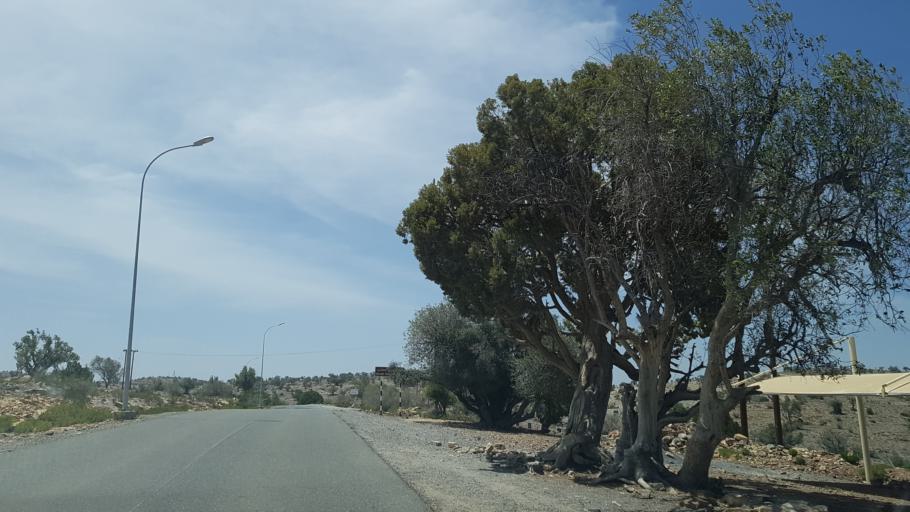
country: OM
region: Al Batinah
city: Bayt al `Awabi
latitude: 23.1216
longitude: 57.6141
